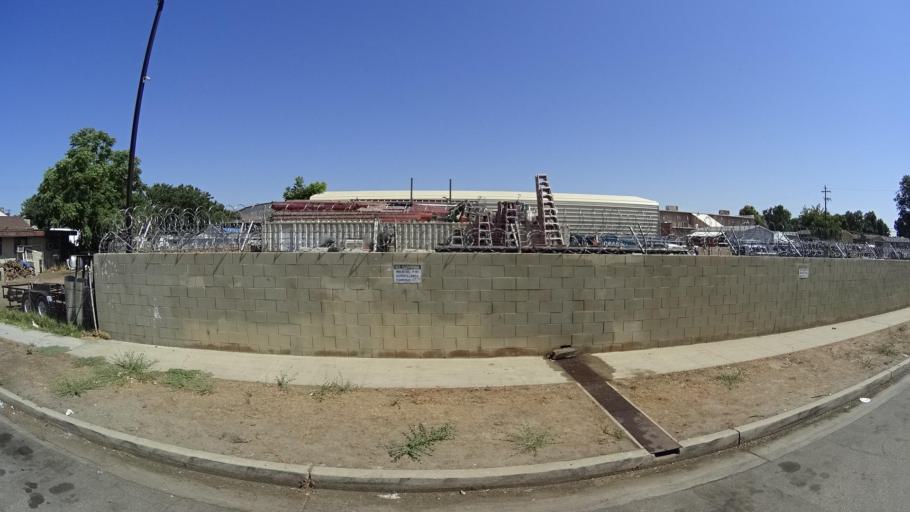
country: US
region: California
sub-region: Fresno County
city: Fresno
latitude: 36.7568
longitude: -119.7417
